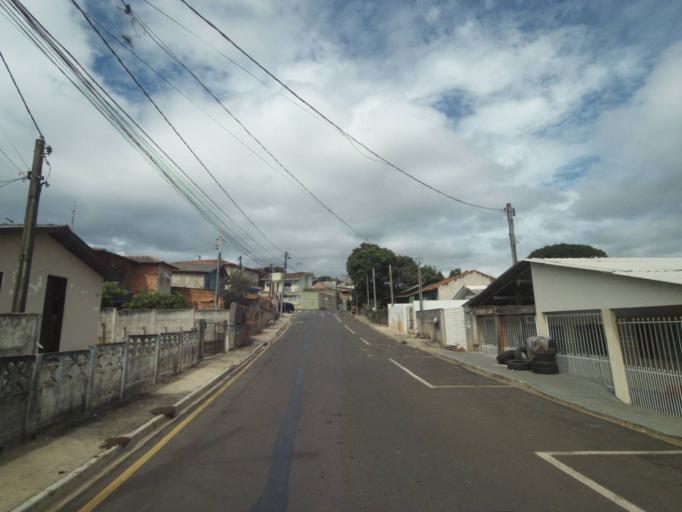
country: BR
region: Parana
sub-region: Telemaco Borba
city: Telemaco Borba
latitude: -24.3321
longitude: -50.6375
